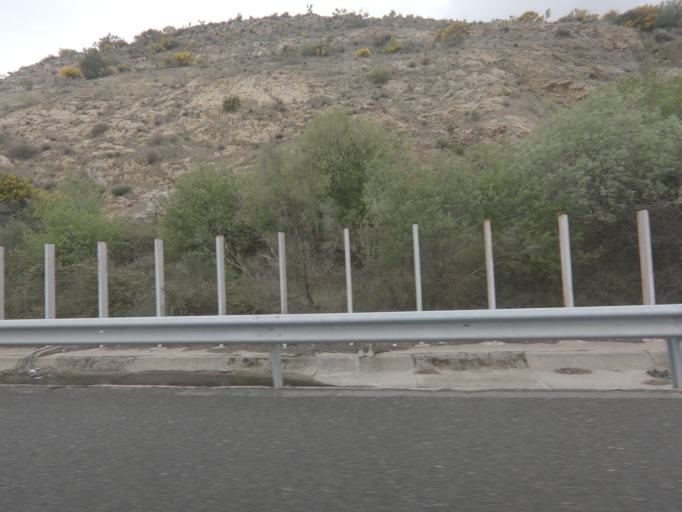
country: ES
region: Extremadura
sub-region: Provincia de Caceres
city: Aldeanueva del Camino
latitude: 40.2822
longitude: -5.9011
